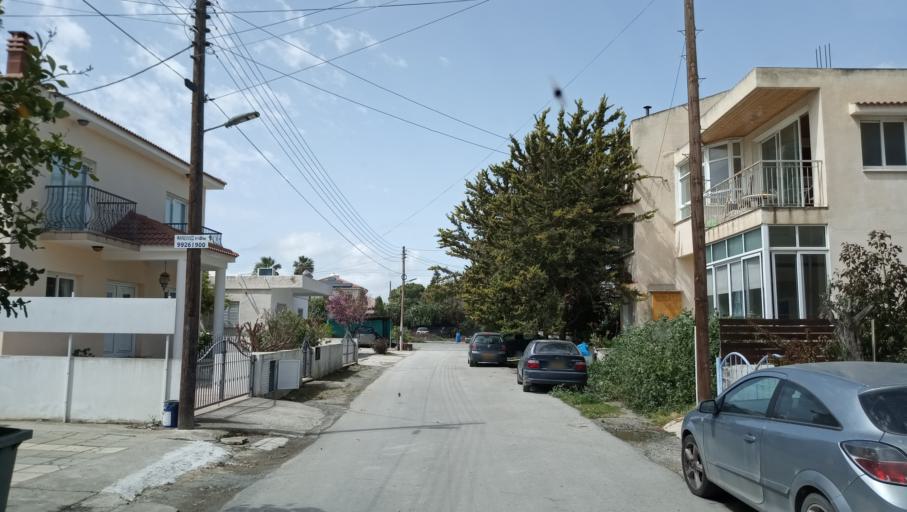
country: CY
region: Lefkosia
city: Dali
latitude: 35.0175
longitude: 33.4188
